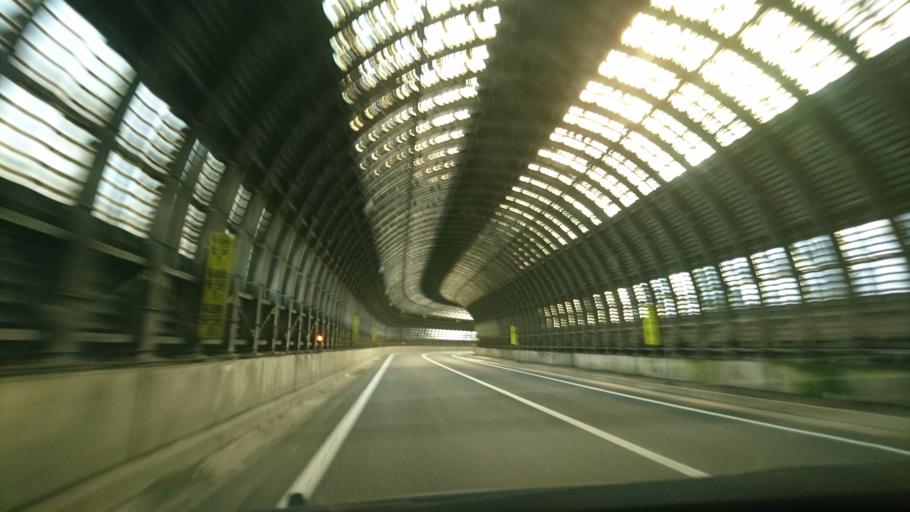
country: JP
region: Iwate
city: Kitakami
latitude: 39.3011
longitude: 140.9007
